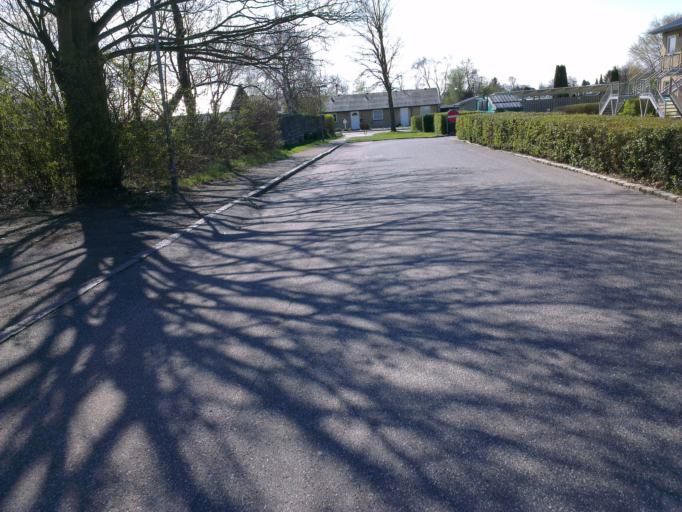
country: DK
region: Capital Region
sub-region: Frederikssund Kommune
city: Frederikssund
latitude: 55.8409
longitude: 12.0732
